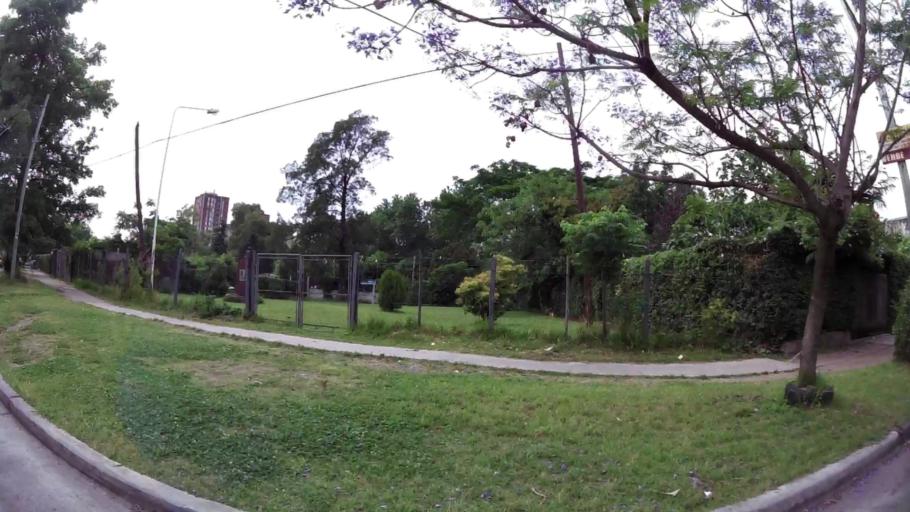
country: AR
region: Buenos Aires F.D.
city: Villa Lugano
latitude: -34.6843
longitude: -58.4944
